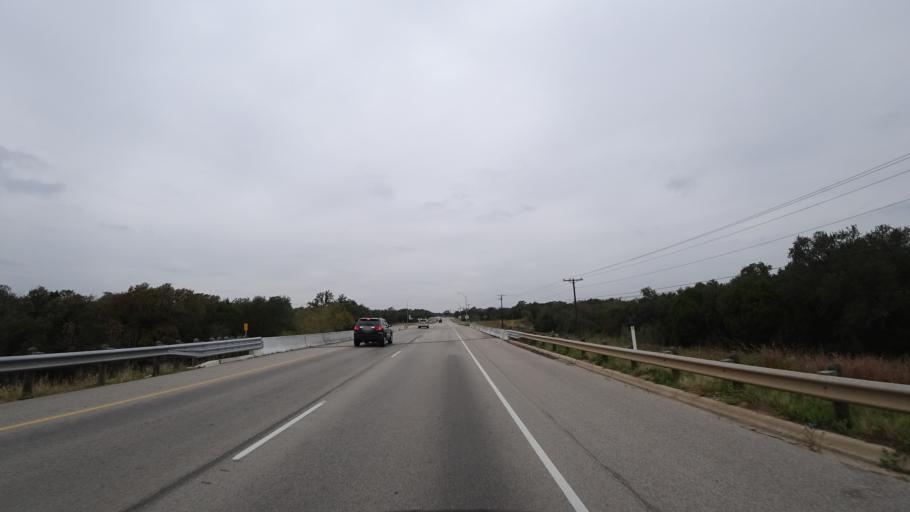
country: US
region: Texas
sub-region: Travis County
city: Shady Hollow
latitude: 30.1864
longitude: -97.9110
